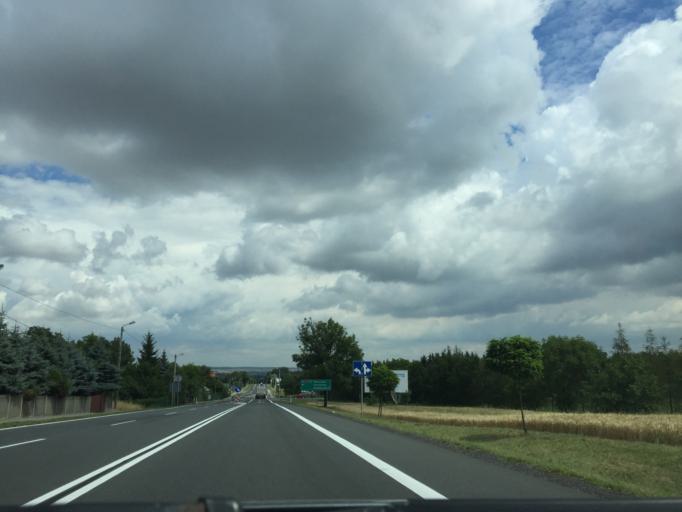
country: PL
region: Lesser Poland Voivodeship
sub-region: Powiat krakowski
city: Michalowice
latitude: 50.2097
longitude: 20.0206
